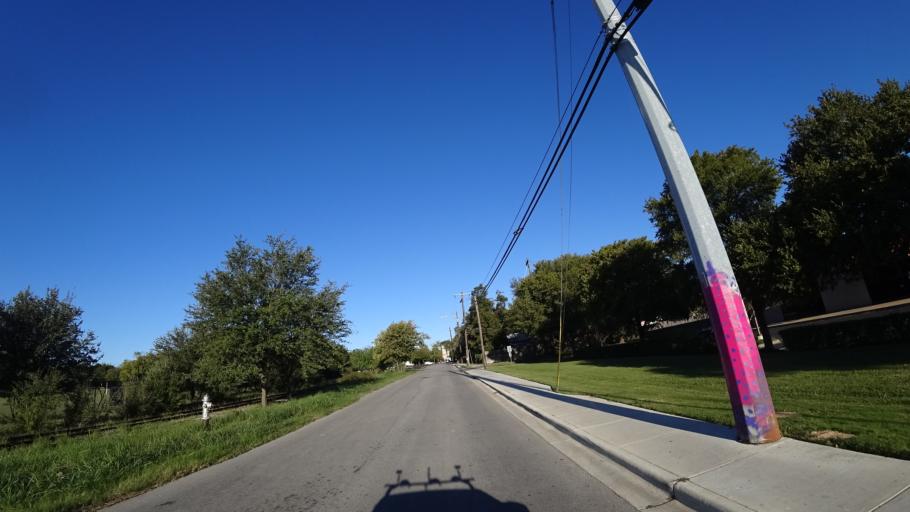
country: US
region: Texas
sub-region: Travis County
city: Austin
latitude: 30.2228
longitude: -97.7677
